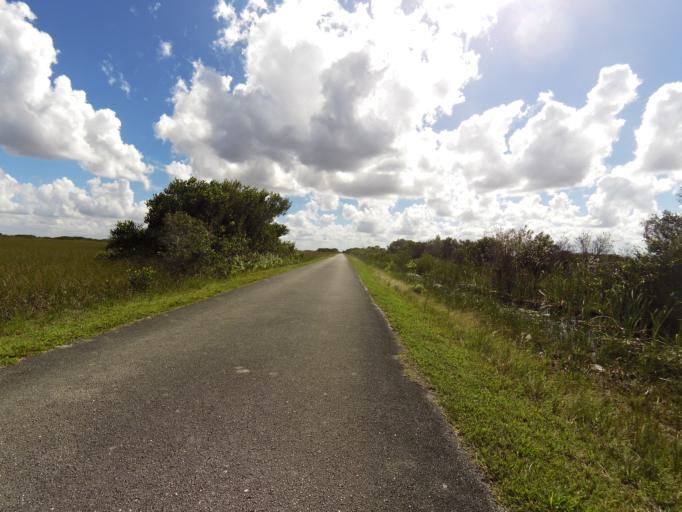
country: US
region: Florida
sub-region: Miami-Dade County
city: The Hammocks
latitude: 25.6924
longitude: -80.7669
